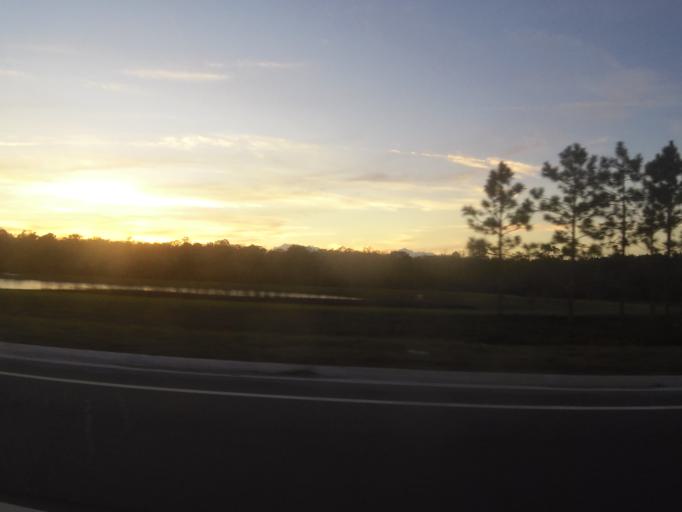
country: US
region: Florida
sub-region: Saint Johns County
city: Fruit Cove
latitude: 30.0945
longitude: -81.5229
